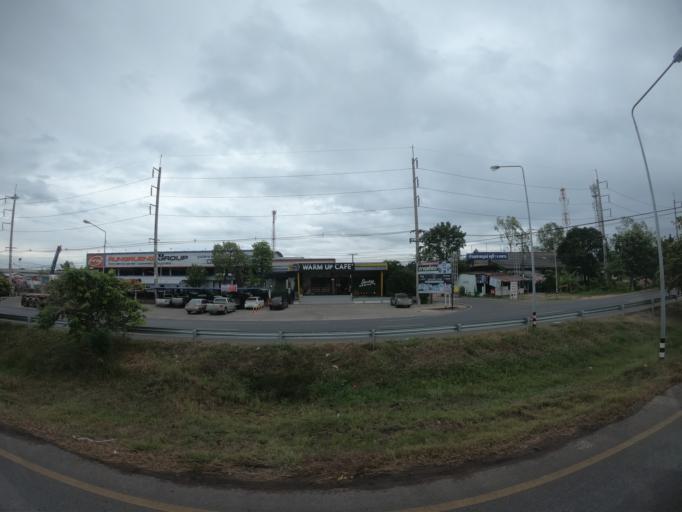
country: TH
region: Roi Et
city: Roi Et
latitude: 16.0485
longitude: 103.6214
